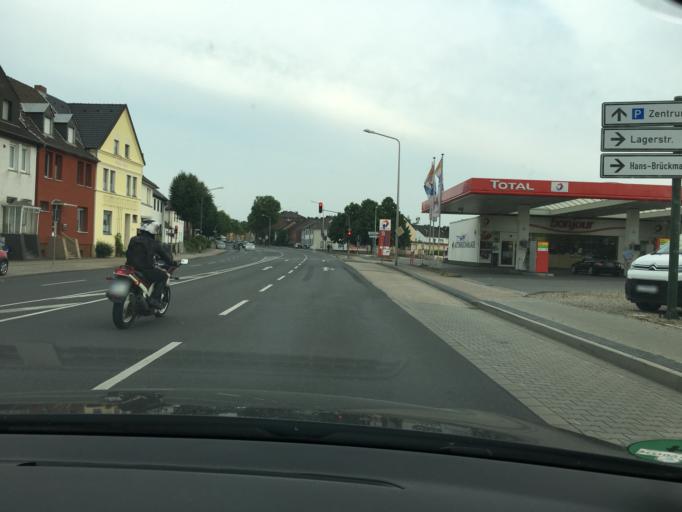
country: DE
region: North Rhine-Westphalia
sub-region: Regierungsbezirk Koln
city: Dueren
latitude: 50.8138
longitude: 6.4886
